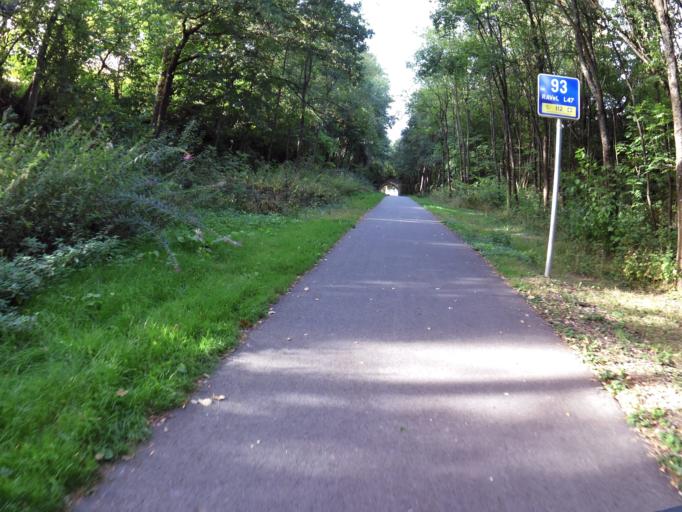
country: BE
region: Wallonia
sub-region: Province de Liege
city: Saint-Vith
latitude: 50.2778
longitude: 6.1319
